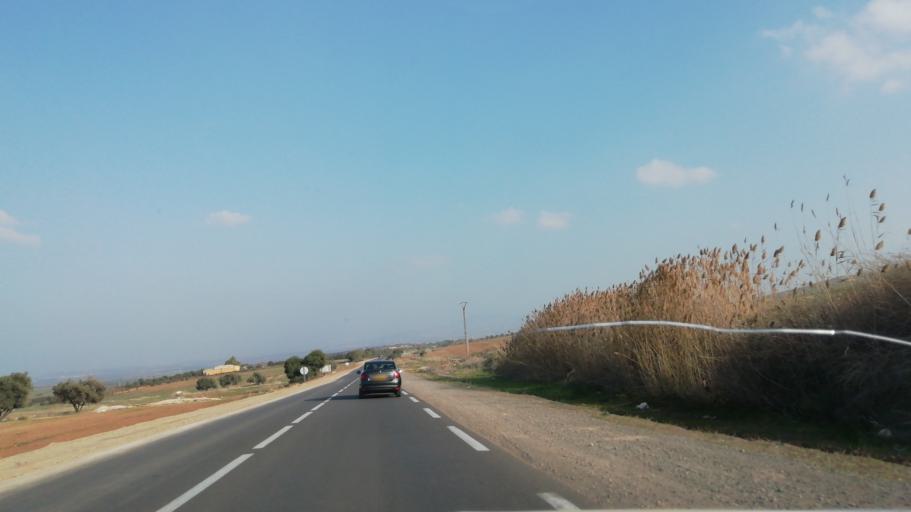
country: DZ
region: Ain Temouchent
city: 'Ain Temouchent
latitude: 35.3050
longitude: -1.0574
